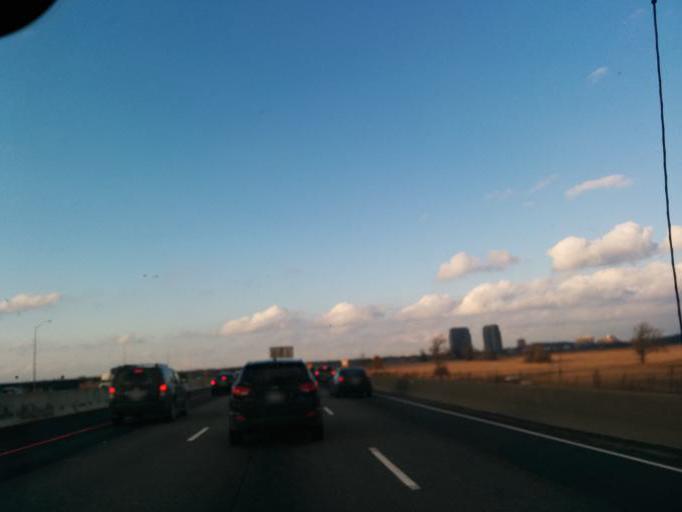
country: CA
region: Ontario
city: Etobicoke
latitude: 43.7081
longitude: -79.6138
